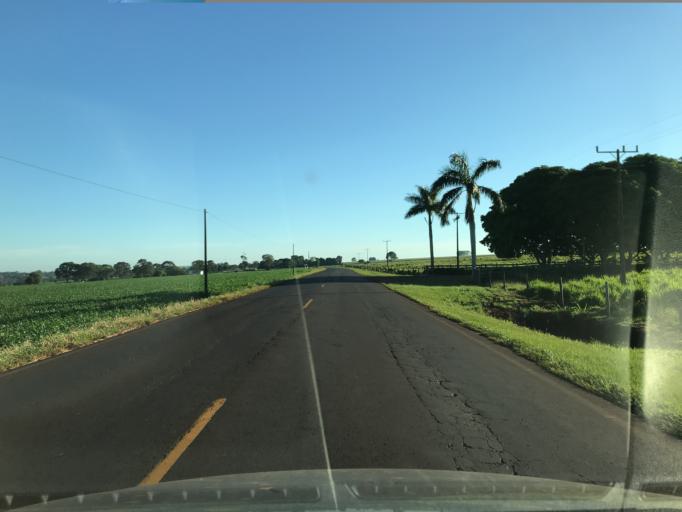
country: BR
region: Parana
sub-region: Ipora
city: Ipora
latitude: -24.1028
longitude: -53.8394
